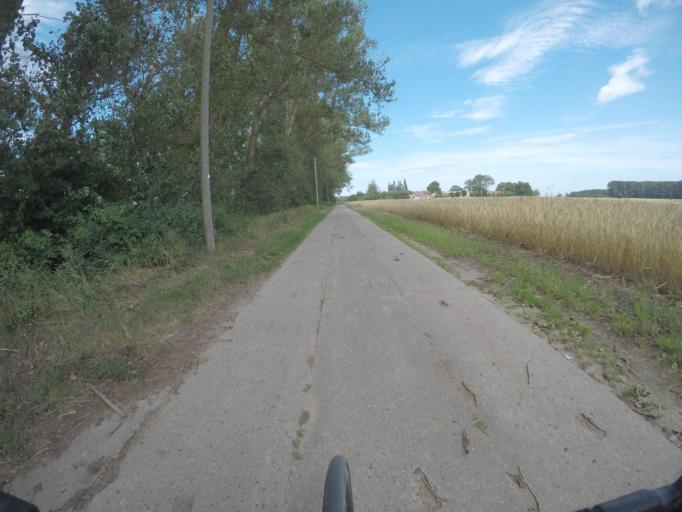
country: DE
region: Mecklenburg-Vorpommern
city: Altefahr
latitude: 54.3676
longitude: 13.1508
